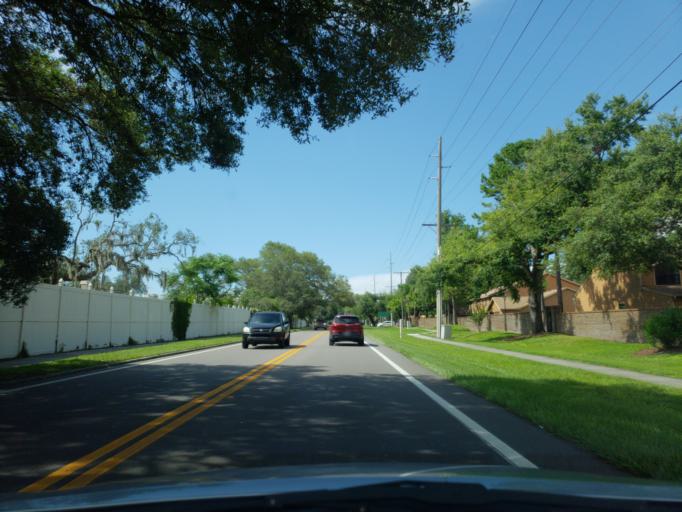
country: US
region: Florida
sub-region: Hillsborough County
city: Carrollwood Village
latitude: 28.0801
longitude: -82.5418
